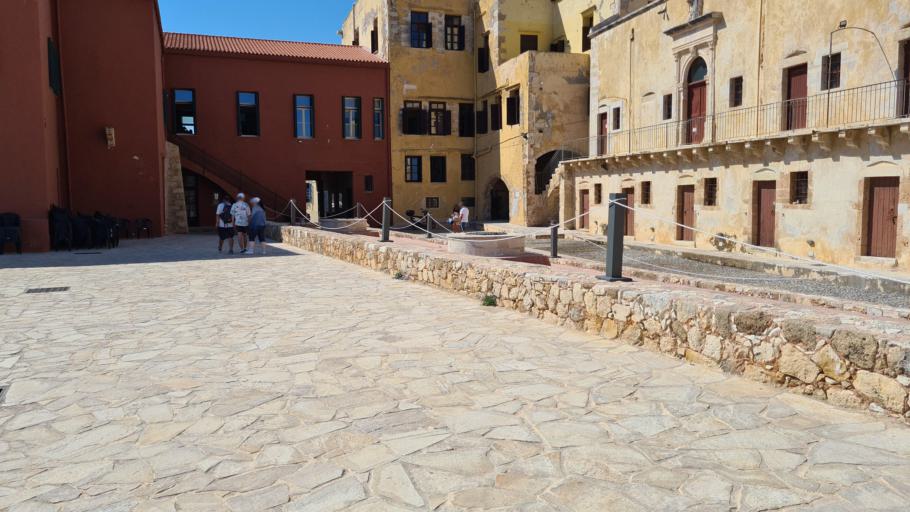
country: GR
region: Crete
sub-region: Nomos Chanias
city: Chania
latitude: 35.5186
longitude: 24.0157
